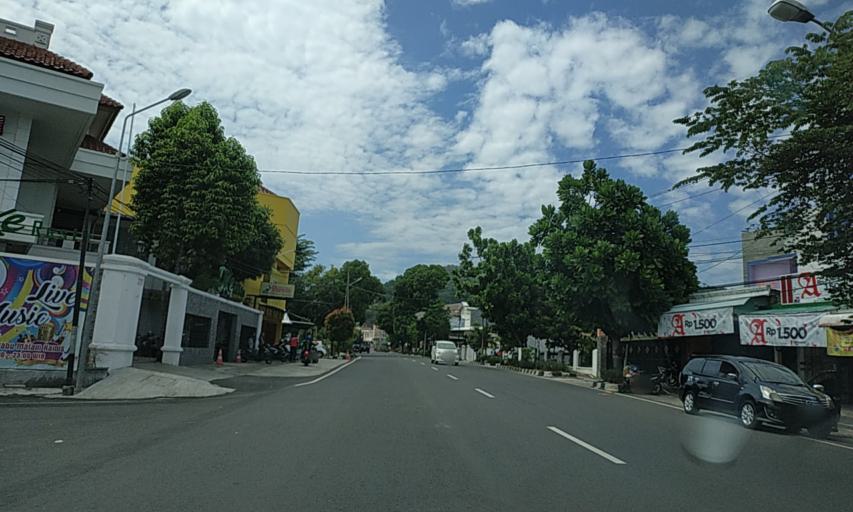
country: ID
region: Central Java
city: Selogiri
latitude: -7.8034
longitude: 110.9137
